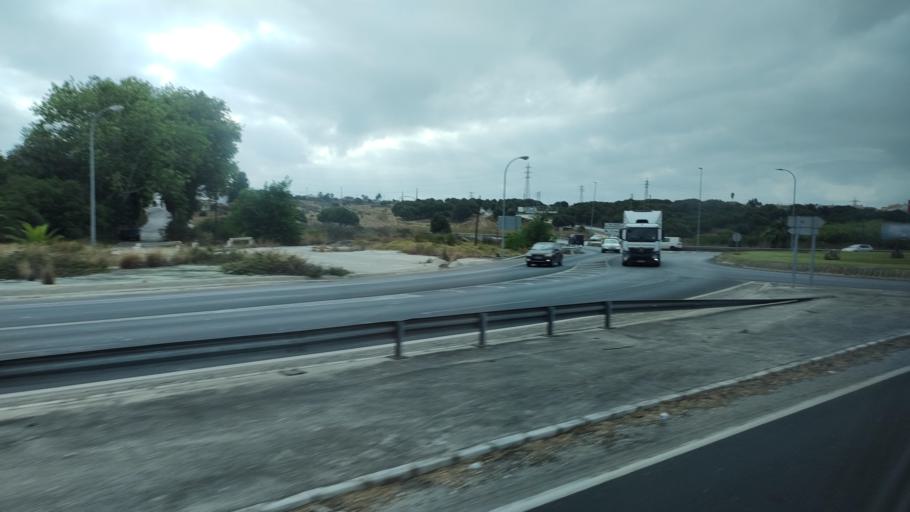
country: ES
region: Andalusia
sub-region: Provincia de Cadiz
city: San Roque
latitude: 36.1828
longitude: -5.3813
